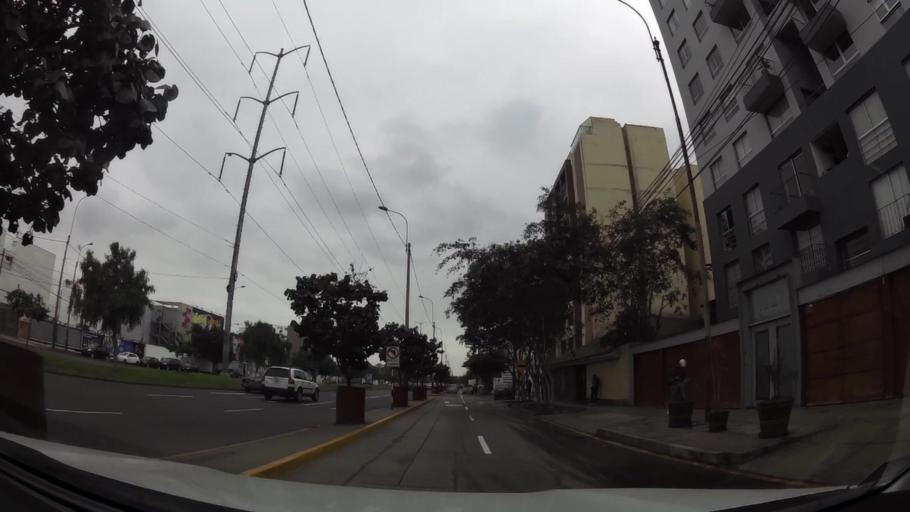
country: PE
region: Lima
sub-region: Lima
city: San Luis
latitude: -12.1102
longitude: -76.9815
